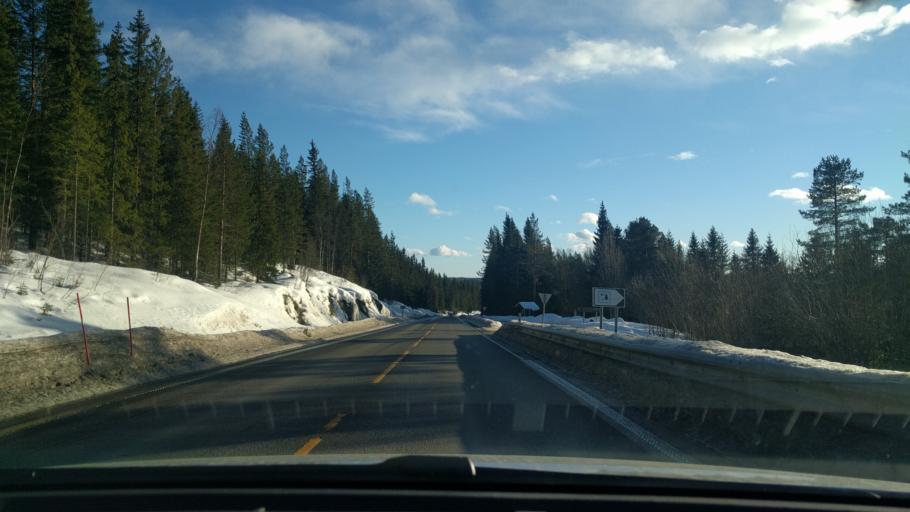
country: NO
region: Hedmark
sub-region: Trysil
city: Innbygda
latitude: 61.0954
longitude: 12.0026
